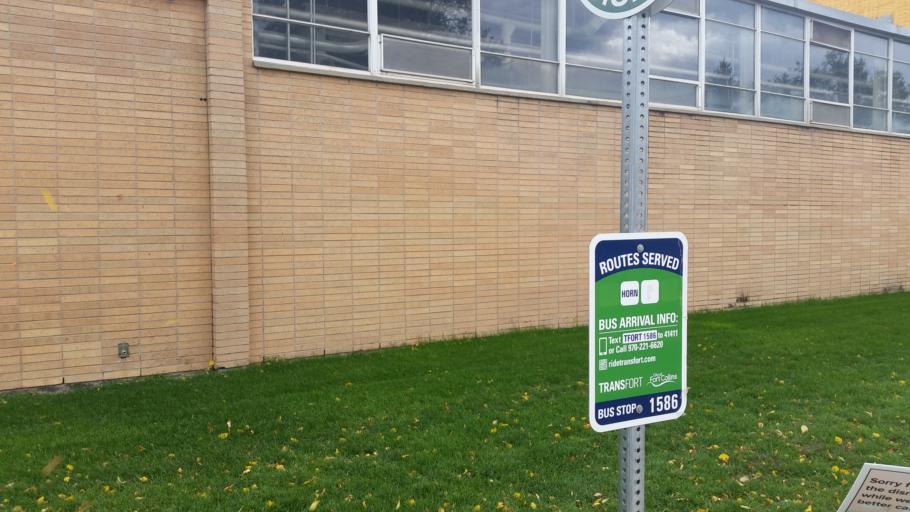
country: US
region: Colorado
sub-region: Larimer County
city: Fort Collins
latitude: 40.5708
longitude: -105.0799
